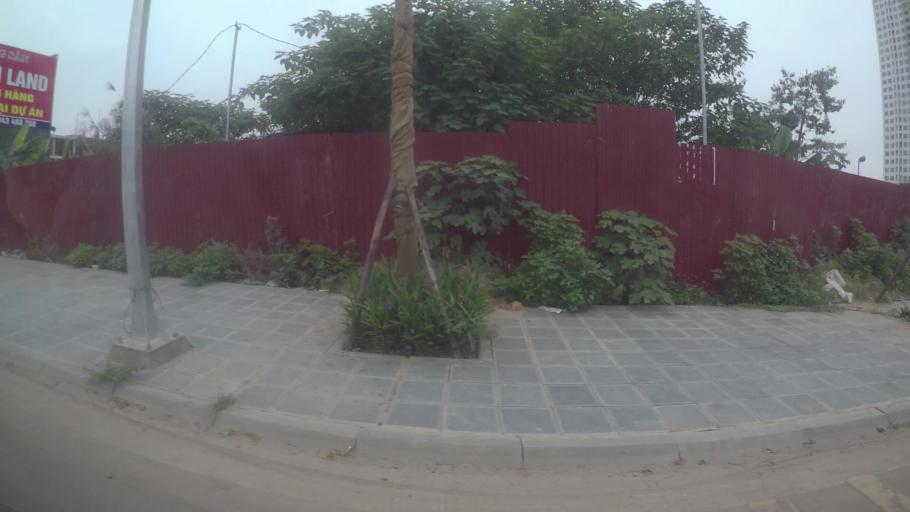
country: VN
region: Ha Noi
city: Ha Dong
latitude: 20.9836
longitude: 105.7412
